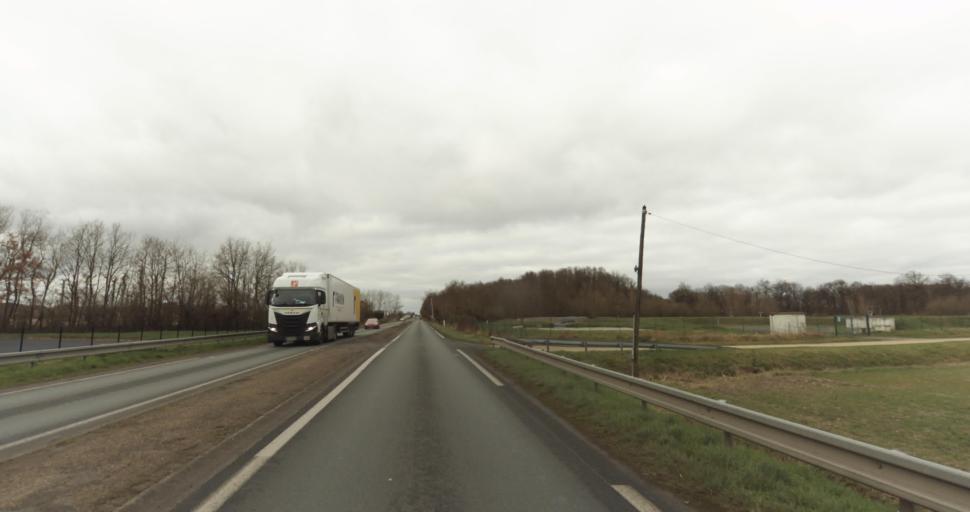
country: FR
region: Pays de la Loire
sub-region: Departement de Maine-et-Loire
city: Vivy
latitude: 47.3324
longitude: -0.0621
